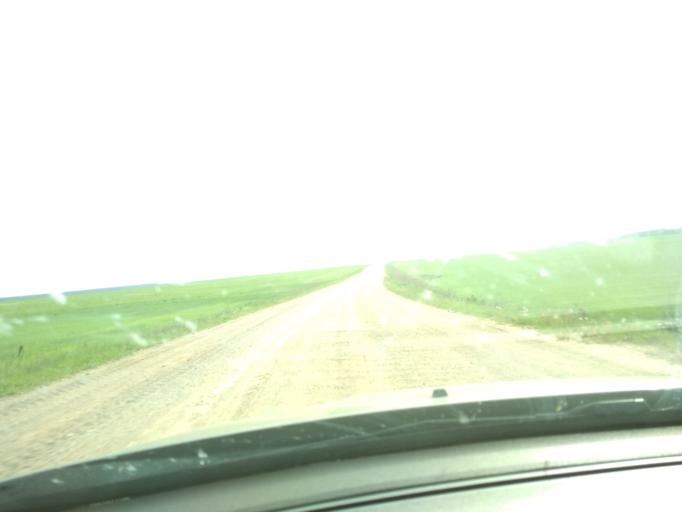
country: BY
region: Grodnenskaya
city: Mir
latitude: 53.3929
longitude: 26.4052
